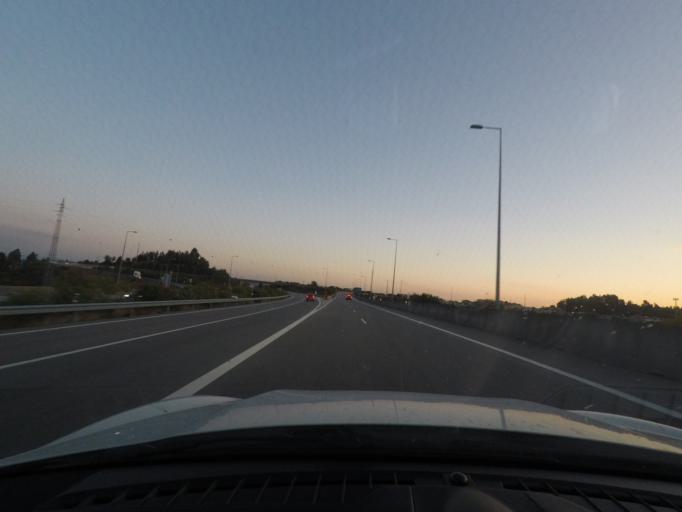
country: PT
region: Porto
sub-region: Lousada
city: Lousada
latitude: 41.2961
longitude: -8.2650
